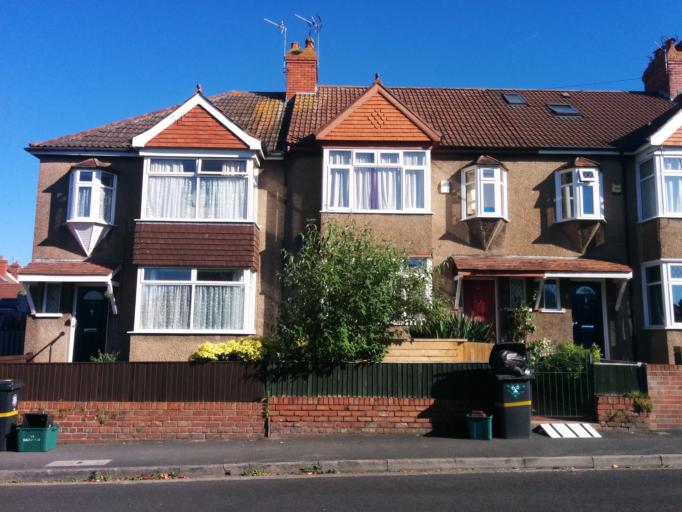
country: GB
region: England
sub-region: Bristol
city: Bristol
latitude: 51.4358
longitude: -2.5751
